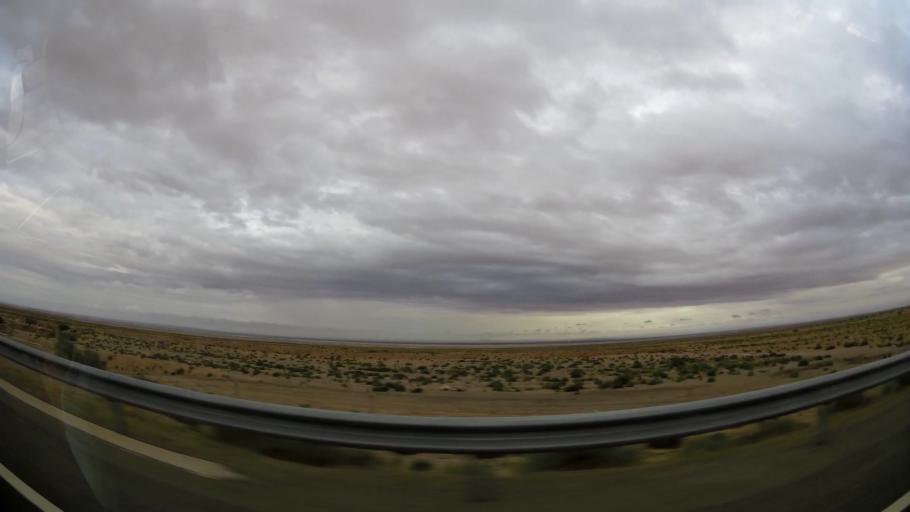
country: MA
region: Taza-Al Hoceima-Taounate
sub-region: Taza
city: Guercif
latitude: 34.3055
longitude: -3.6207
